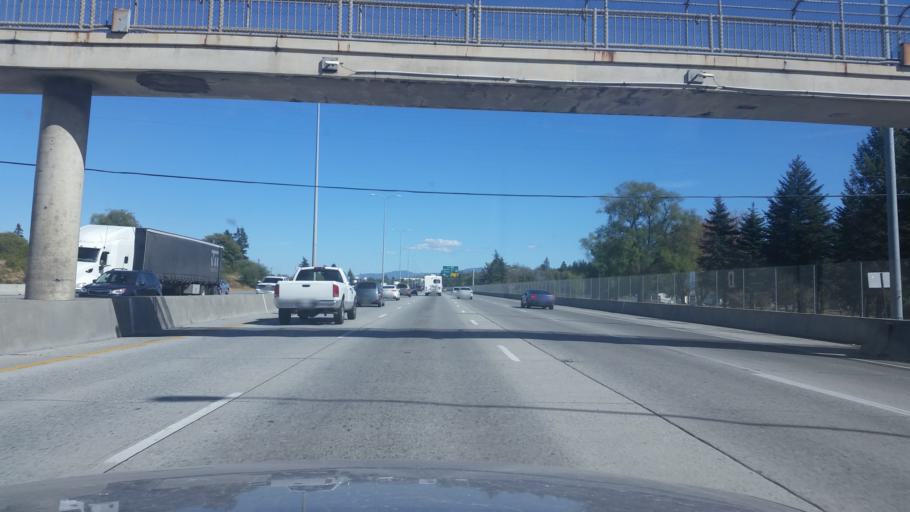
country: US
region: Washington
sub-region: Spokane County
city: Millwood
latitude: 47.6538
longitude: -117.3424
